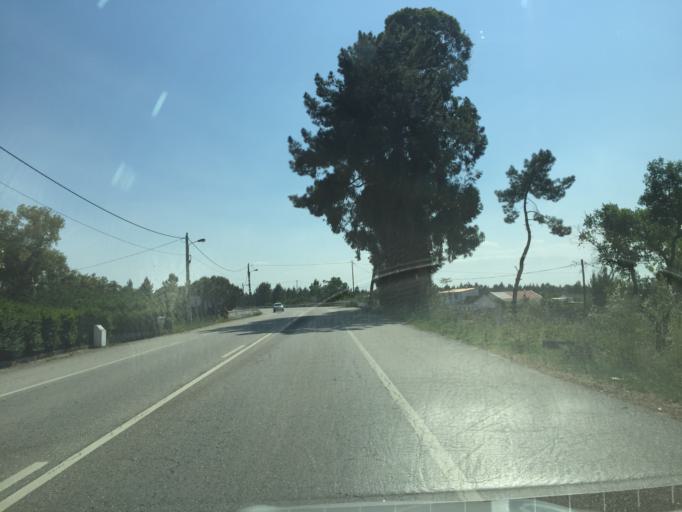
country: PT
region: Santarem
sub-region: Chamusca
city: Vila Nova da Barquinha
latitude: 39.4126
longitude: -8.4238
